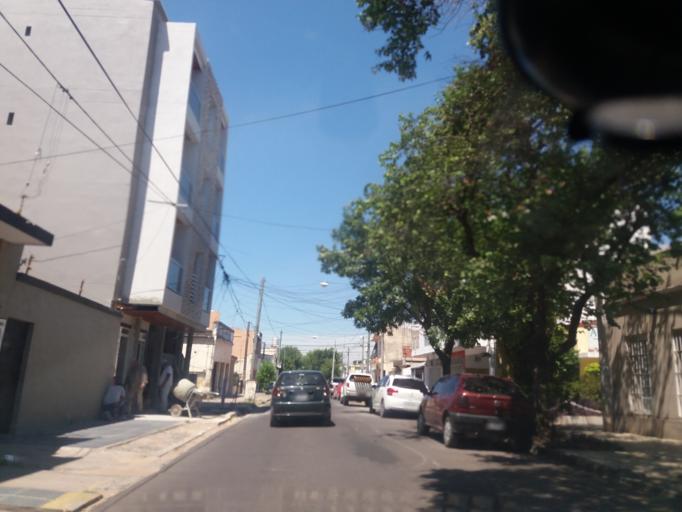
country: AR
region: Corrientes
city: Corrientes
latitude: -27.4777
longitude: -58.8447
